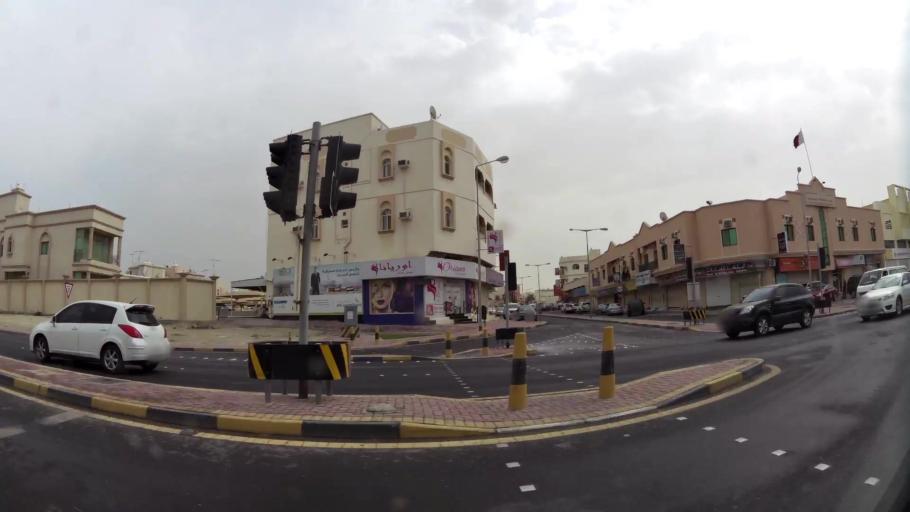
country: BH
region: Northern
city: Ar Rifa'
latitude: 26.1352
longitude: 50.5538
